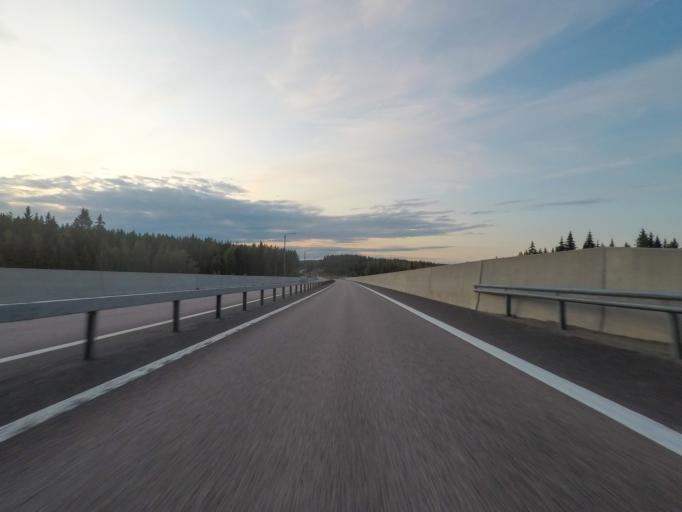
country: FI
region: Central Finland
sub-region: Jyvaeskylae
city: Saeynaetsalo
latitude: 62.1881
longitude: 25.9034
